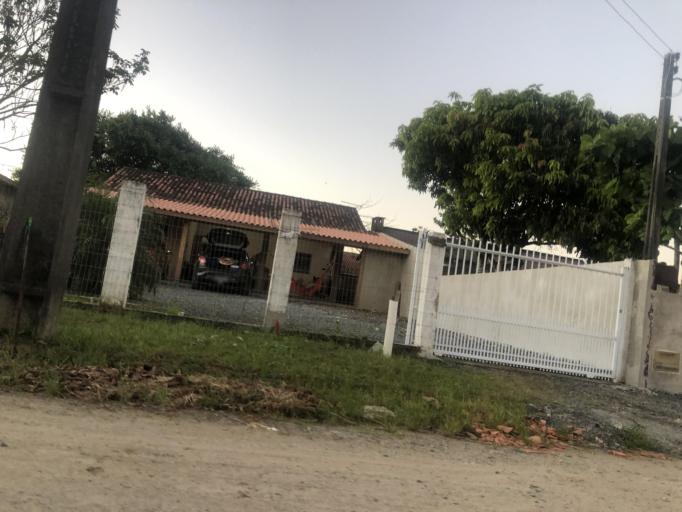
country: BR
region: Santa Catarina
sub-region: Sao Francisco Do Sul
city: Sao Francisco do Sul
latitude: -26.2111
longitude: -48.5304
